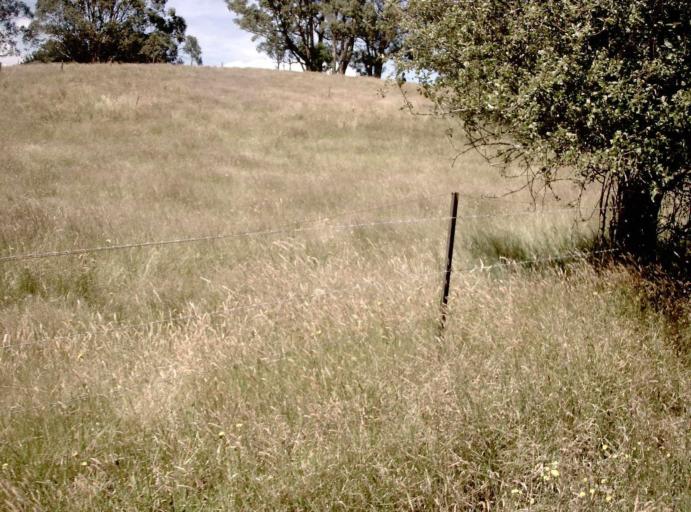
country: AU
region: Victoria
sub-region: Baw Baw
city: Warragul
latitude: -37.8750
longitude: 146.0963
